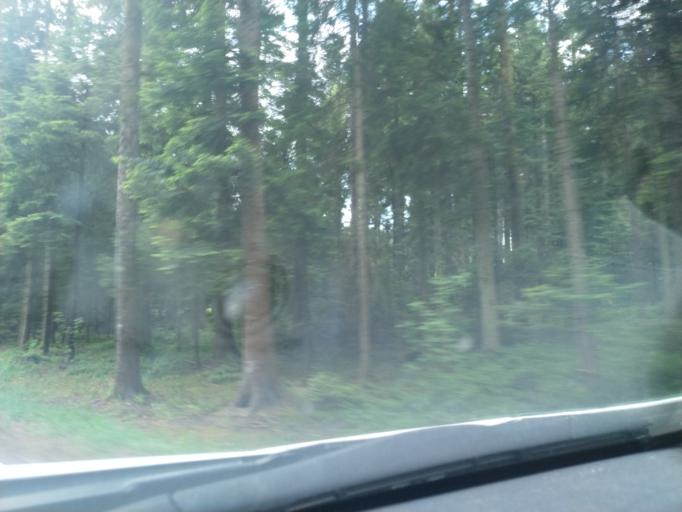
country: DE
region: Baden-Wuerttemberg
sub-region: Karlsruhe Region
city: Baiersbronn
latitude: 48.5773
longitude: 8.4232
